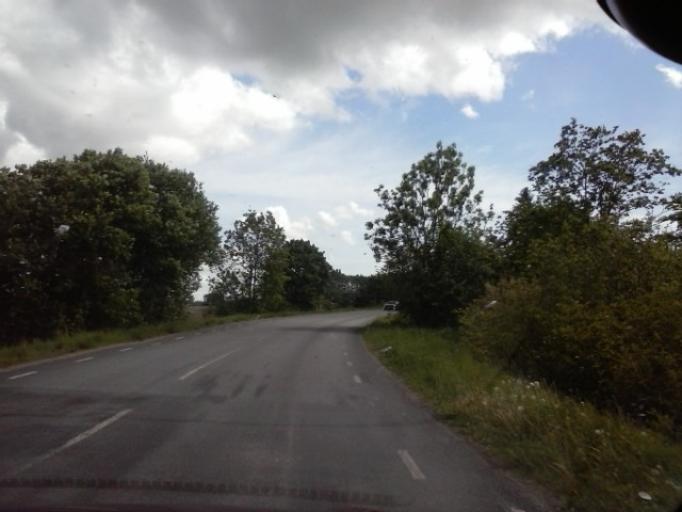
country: EE
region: Laeaene
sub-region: Ridala Parish
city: Uuemoisa
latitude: 58.9627
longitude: 23.7826
